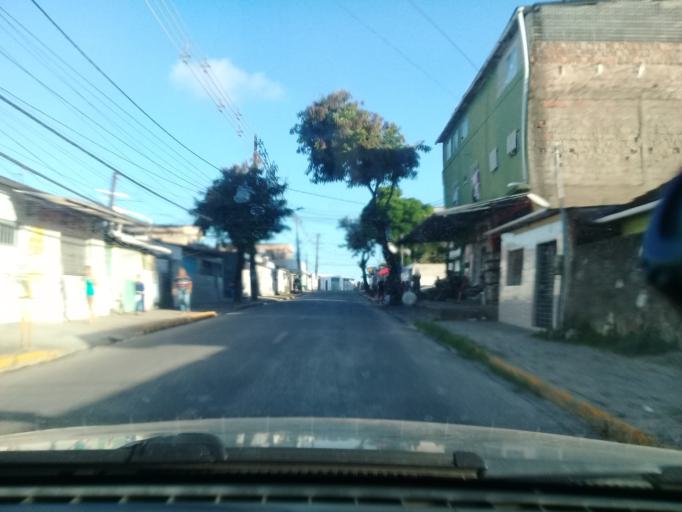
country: BR
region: Pernambuco
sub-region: Jaboatao Dos Guararapes
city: Jaboatao dos Guararapes
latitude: -8.1210
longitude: -34.9540
